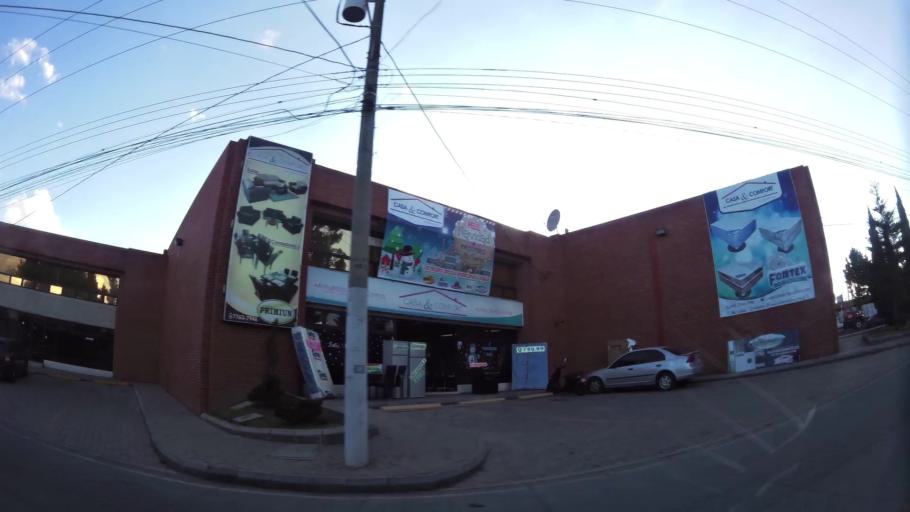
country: GT
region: Quetzaltenango
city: Quetzaltenango
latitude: 14.8546
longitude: -91.5352
